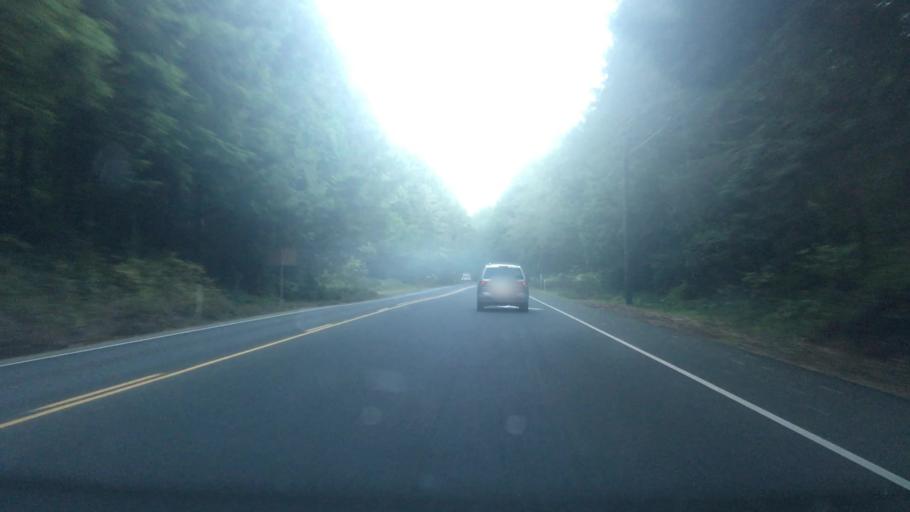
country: US
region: Oregon
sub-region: Clatsop County
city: Cannon Beach
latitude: 45.7857
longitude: -123.9584
